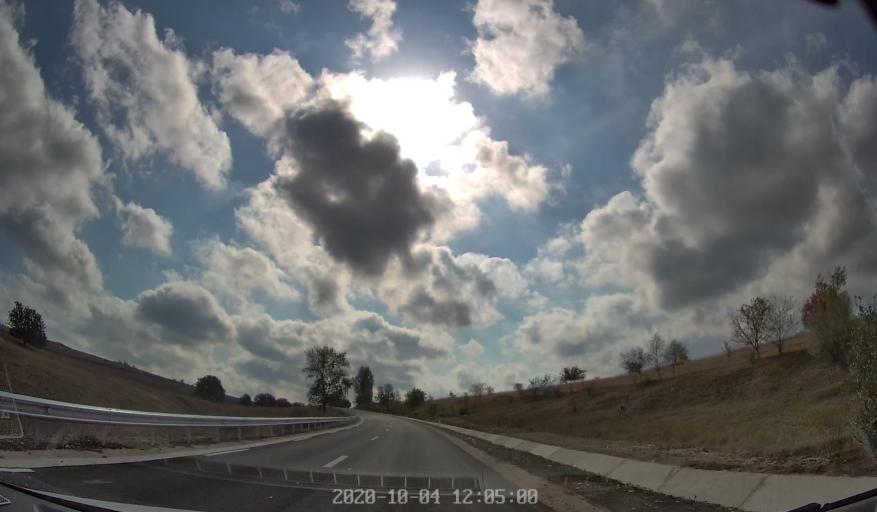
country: MD
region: Rezina
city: Saharna
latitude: 47.5984
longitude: 28.9479
